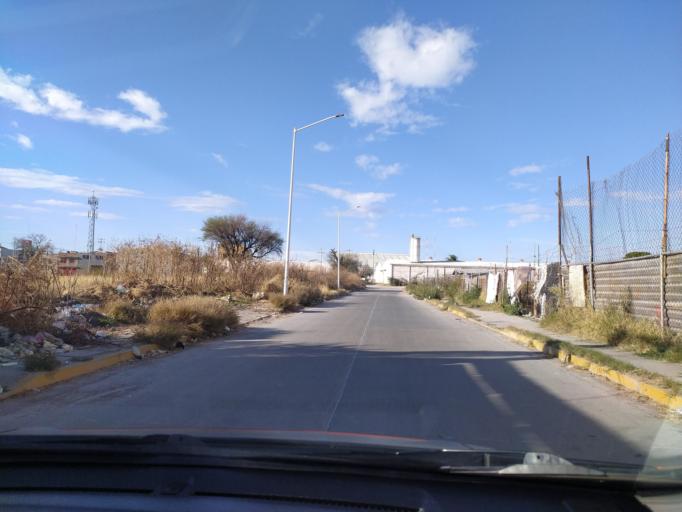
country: MX
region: Guanajuato
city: San Francisco del Rincon
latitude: 21.0269
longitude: -101.8535
